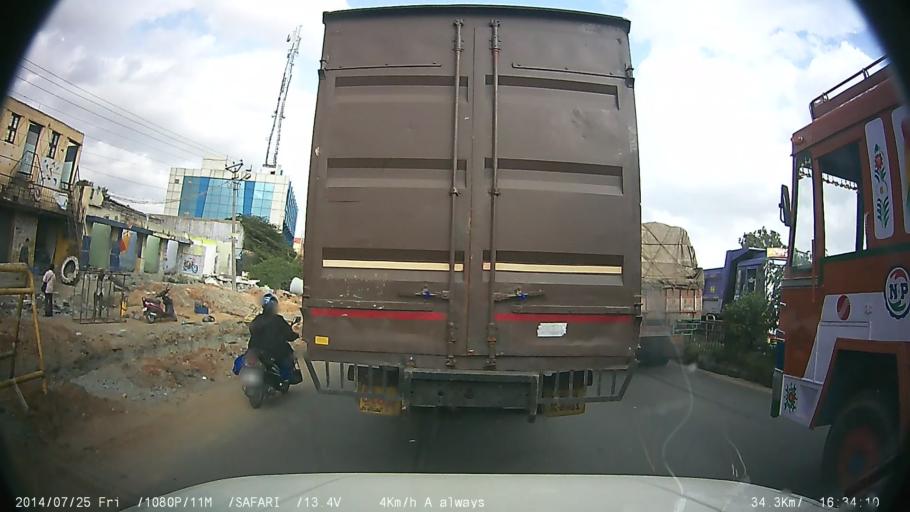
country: IN
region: Tamil Nadu
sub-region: Krishnagiri
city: Hosur
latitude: 12.7652
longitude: 77.7910
